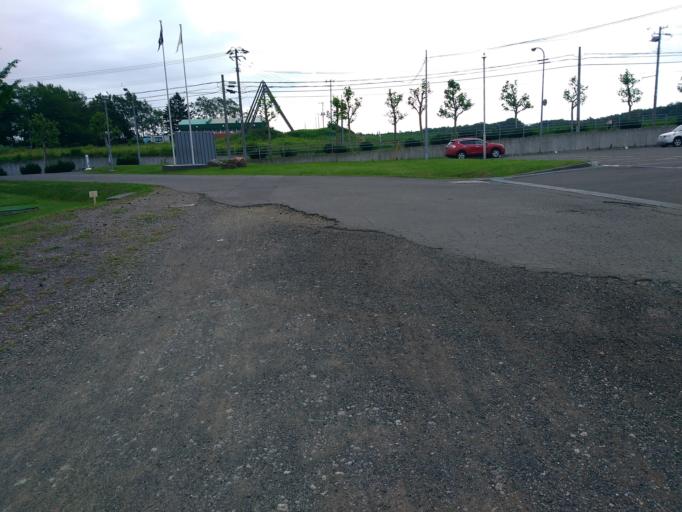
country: JP
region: Hokkaido
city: Ebetsu
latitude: 43.0682
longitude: 141.5013
